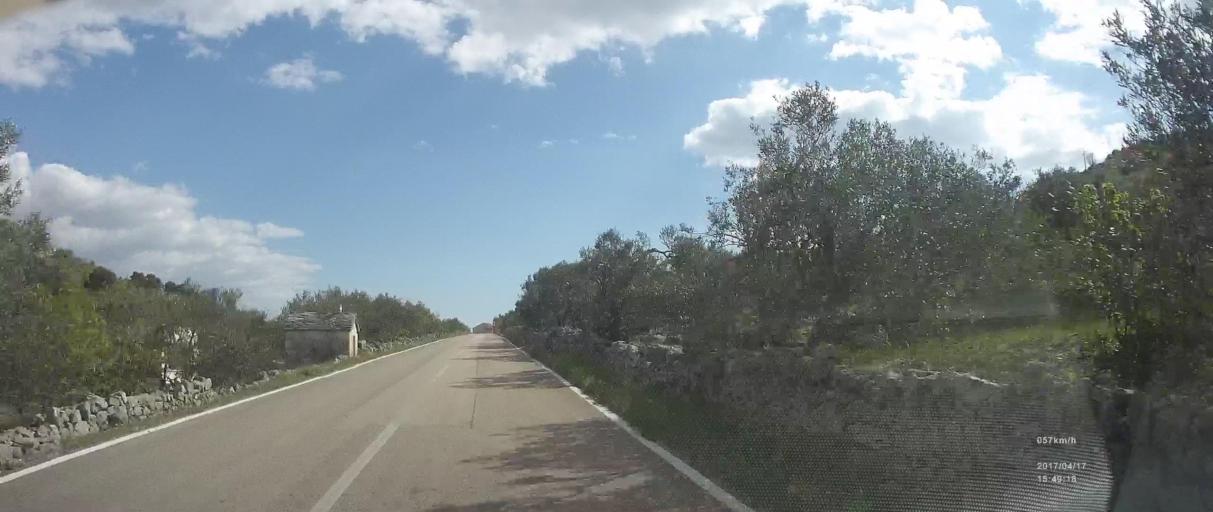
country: HR
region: Sibensko-Kniniska
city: Primosten
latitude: 43.6151
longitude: 15.9763
